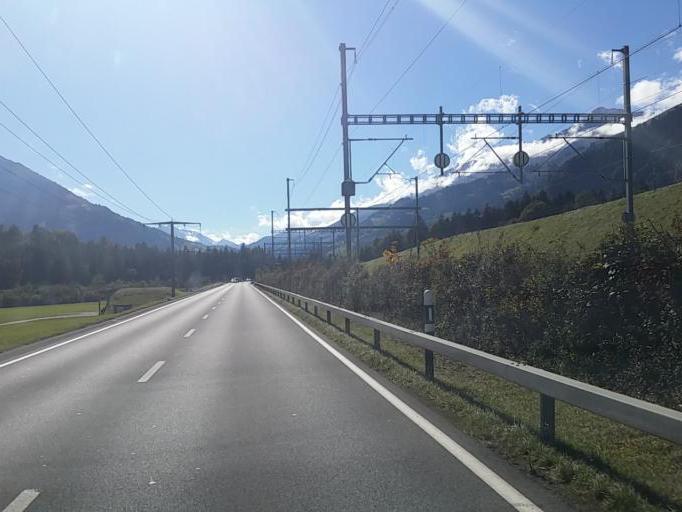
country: CH
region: Bern
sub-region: Frutigen-Niedersimmental District
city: Frutigen
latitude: 46.6118
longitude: 7.6737
